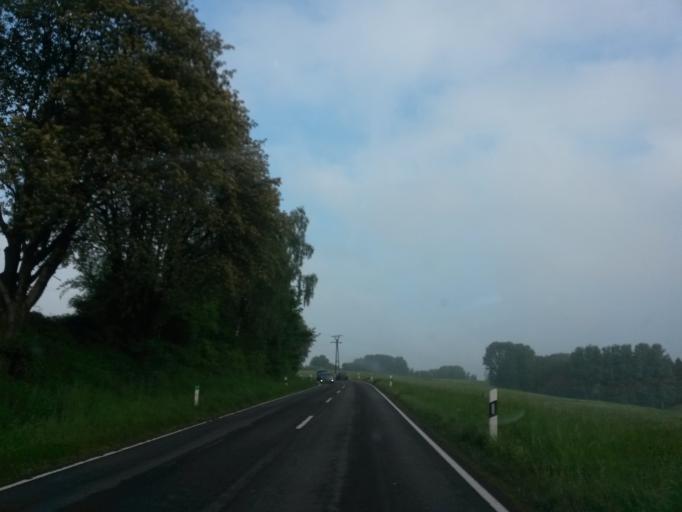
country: DE
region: North Rhine-Westphalia
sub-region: Regierungsbezirk Koln
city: Hennef
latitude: 50.8466
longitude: 7.3057
